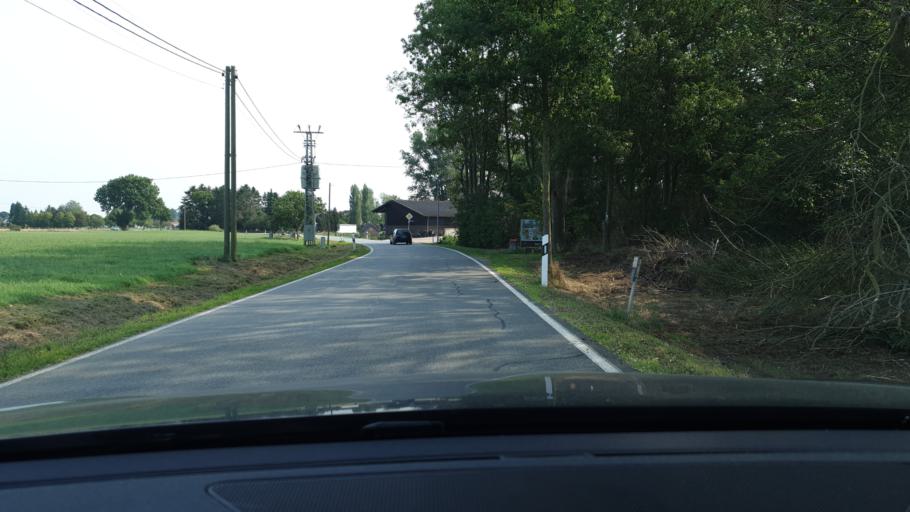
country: DE
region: North Rhine-Westphalia
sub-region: Regierungsbezirk Dusseldorf
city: Kranenburg
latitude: 51.8481
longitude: 6.0610
